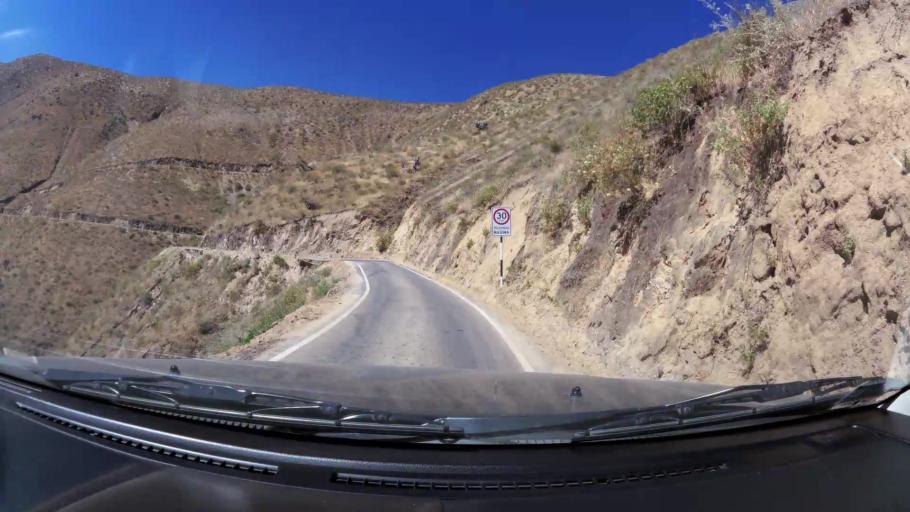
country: PE
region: Ica
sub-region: Provincia de Pisco
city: Huancano
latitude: -13.7220
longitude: -75.4534
